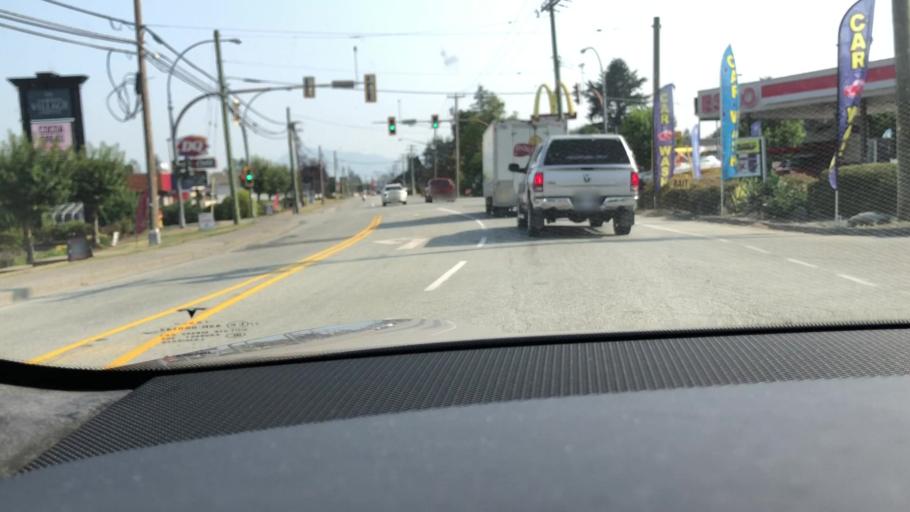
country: CA
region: British Columbia
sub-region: Fraser Valley Regional District
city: Chilliwack
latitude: 49.1062
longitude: -121.9606
